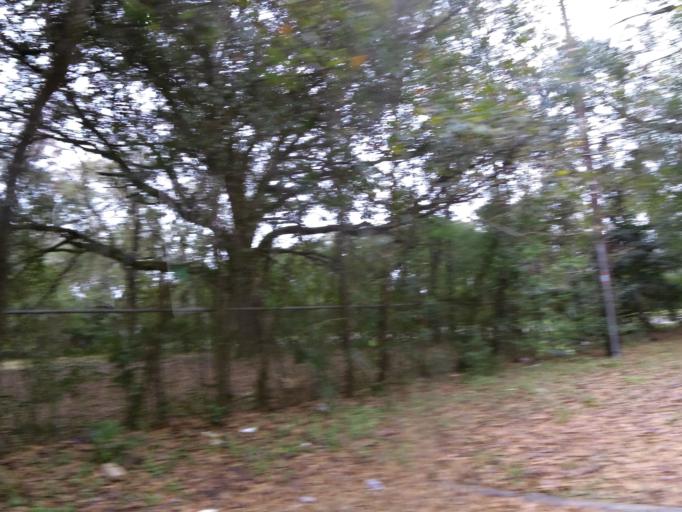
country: US
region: Florida
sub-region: Duval County
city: Jacksonville
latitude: 30.3572
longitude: -81.7034
